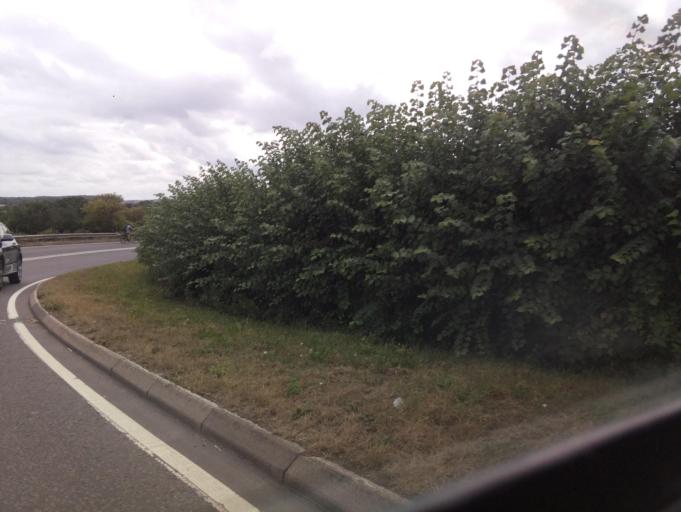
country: GB
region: England
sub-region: Leicestershire
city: Castle Donington
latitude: 52.8134
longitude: -1.3771
